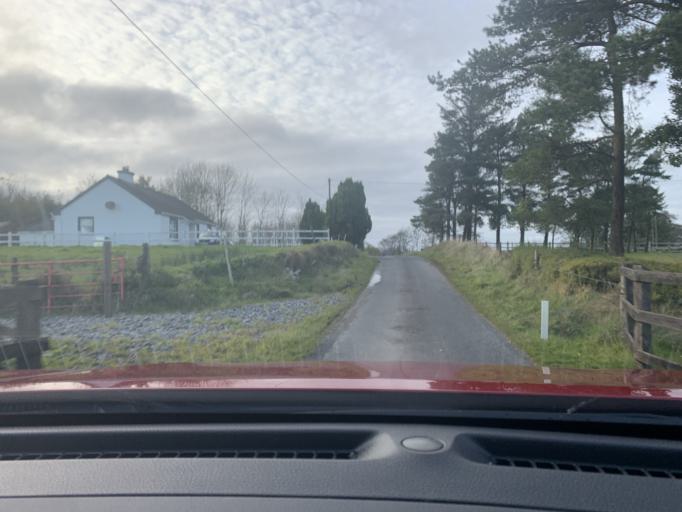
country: IE
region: Connaught
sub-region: Roscommon
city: Ballaghaderreen
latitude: 53.9707
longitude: -8.6209
